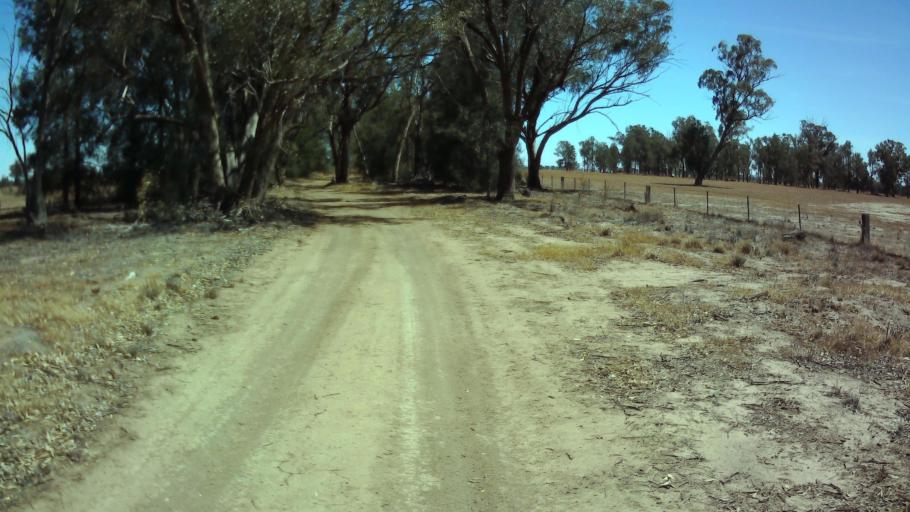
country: AU
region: New South Wales
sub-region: Bland
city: West Wyalong
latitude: -33.9142
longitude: 147.6839
